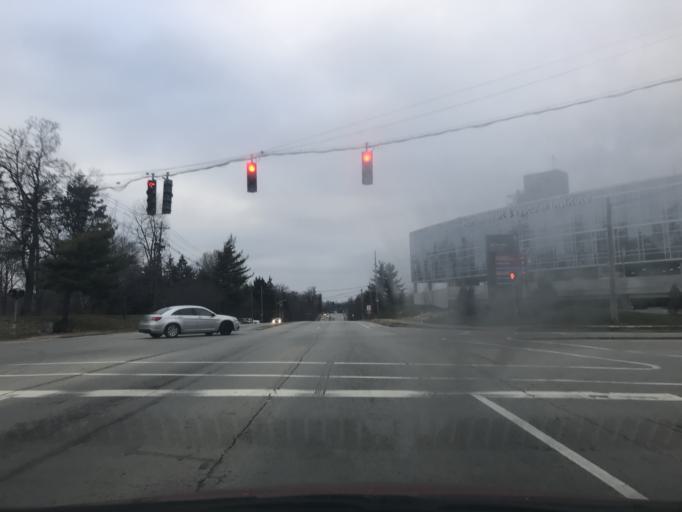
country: US
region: Kentucky
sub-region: Jefferson County
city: Audubon Park
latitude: 38.2139
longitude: -85.7228
